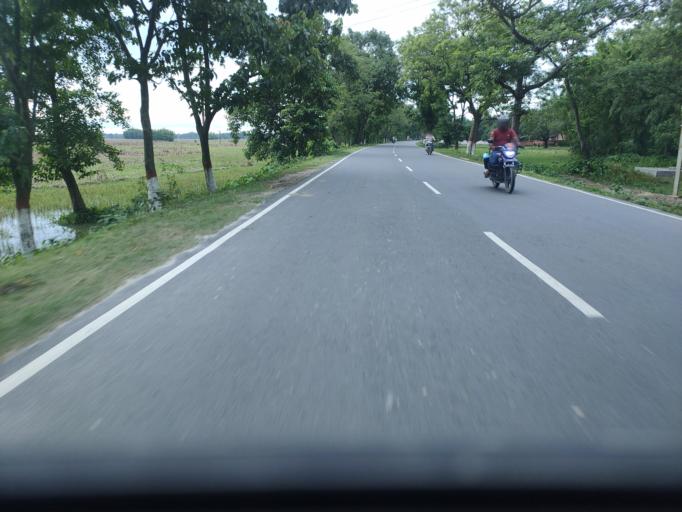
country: IN
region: West Bengal
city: Kishanganj
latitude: 26.1732
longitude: 87.9117
